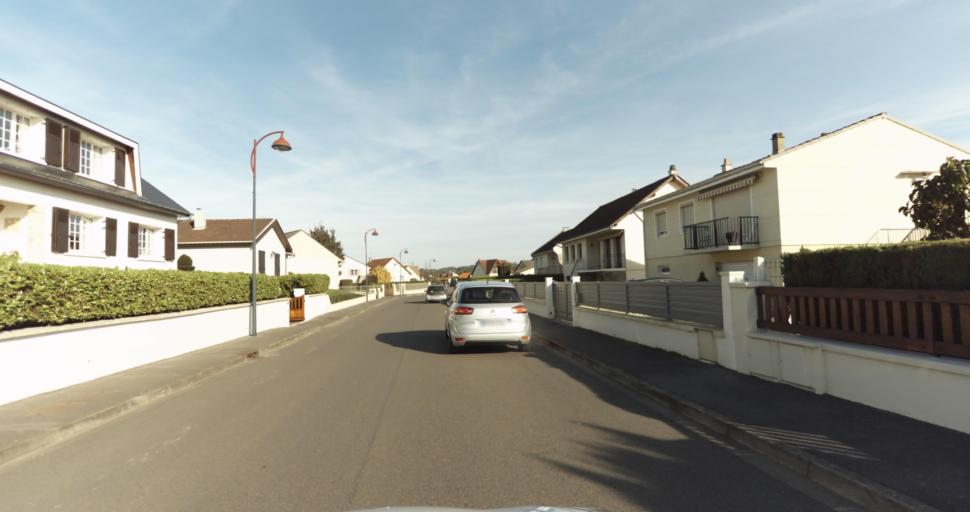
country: FR
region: Champagne-Ardenne
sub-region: Departement des Ardennes
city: Villers-Semeuse
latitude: 49.7458
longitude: 4.7470
